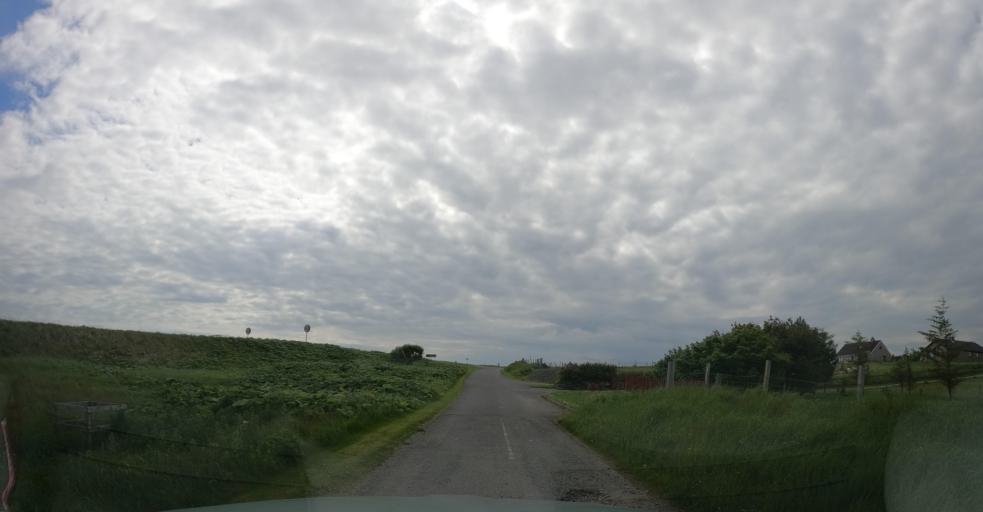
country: GB
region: Scotland
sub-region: Eilean Siar
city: Isle of Lewis
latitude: 58.2867
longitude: -6.2842
